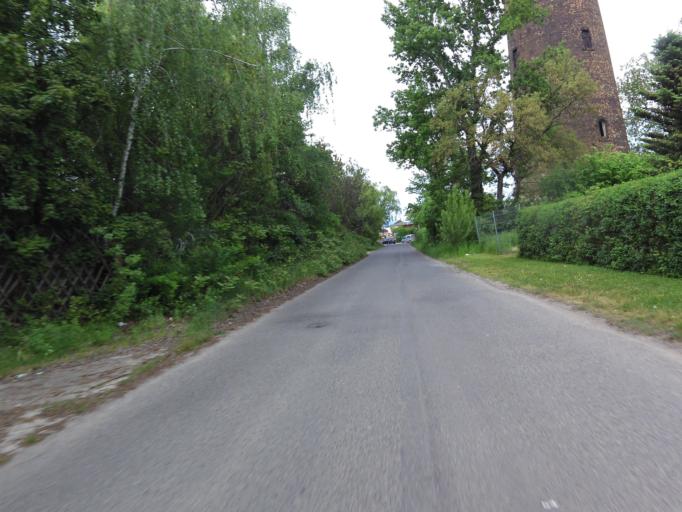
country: DE
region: Saxony
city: Markkleeberg
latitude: 51.2999
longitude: 12.3126
